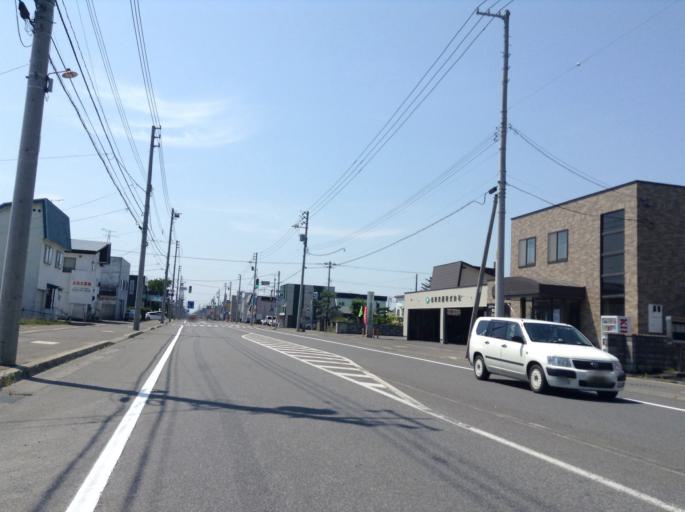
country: JP
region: Hokkaido
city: Nayoro
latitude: 44.3599
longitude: 142.4572
